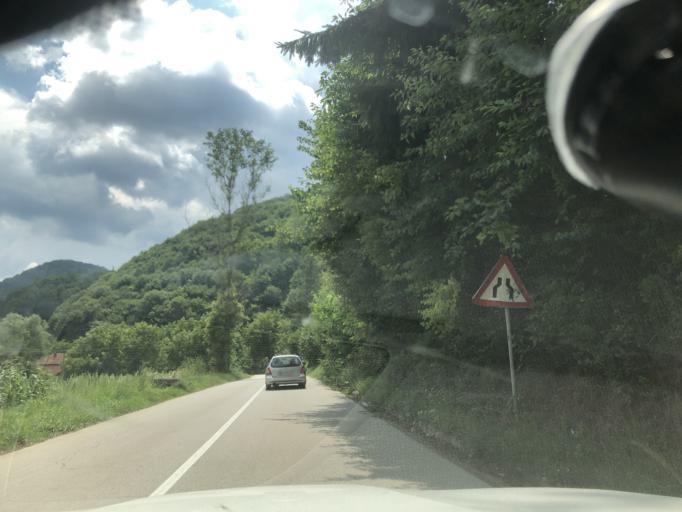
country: RS
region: Central Serbia
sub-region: Jablanicki Okrug
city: Medvega
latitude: 42.7896
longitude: 21.5827
